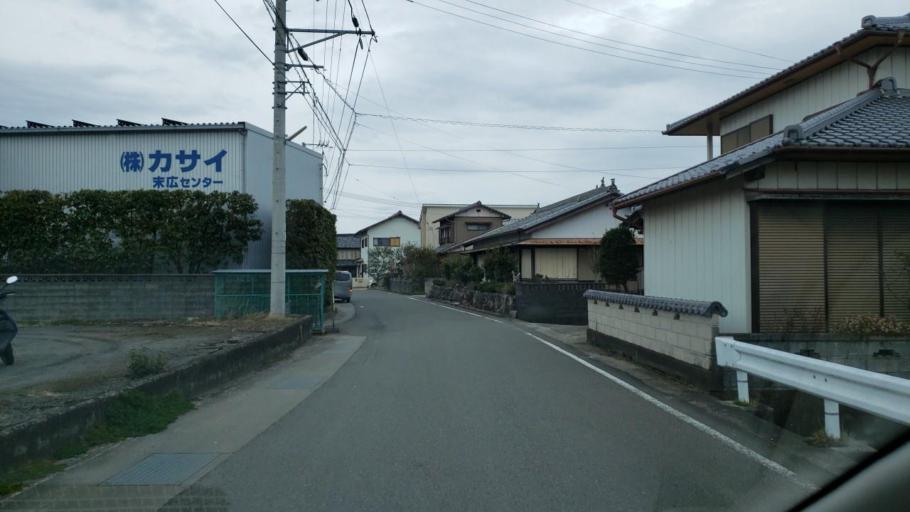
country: JP
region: Tokushima
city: Kamojimacho-jogejima
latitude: 34.0908
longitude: 134.2990
